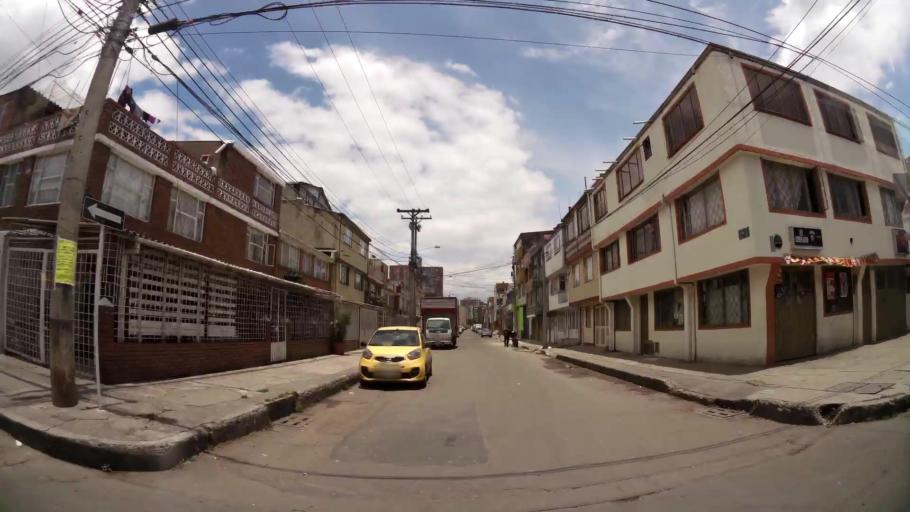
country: CO
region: Bogota D.C.
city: Barrio San Luis
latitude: 4.7140
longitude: -74.0613
